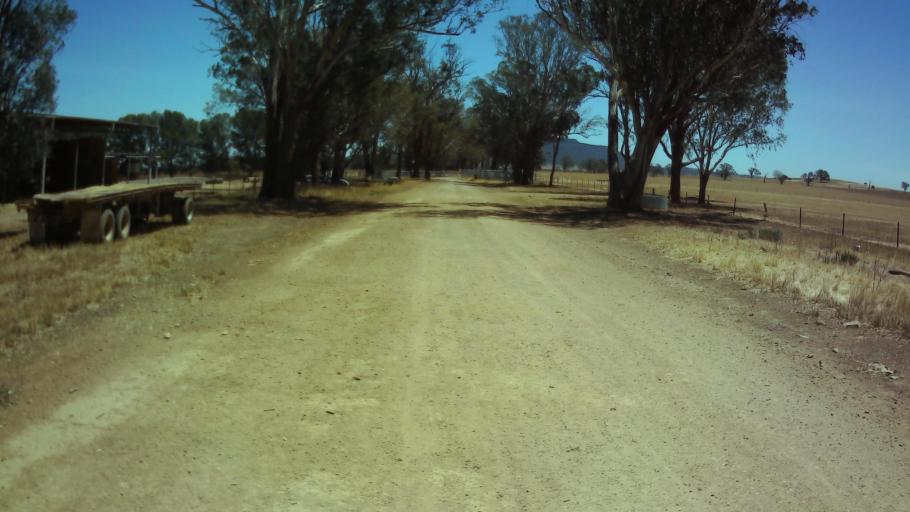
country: AU
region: New South Wales
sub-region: Weddin
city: Grenfell
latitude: -34.0110
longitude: 148.1701
